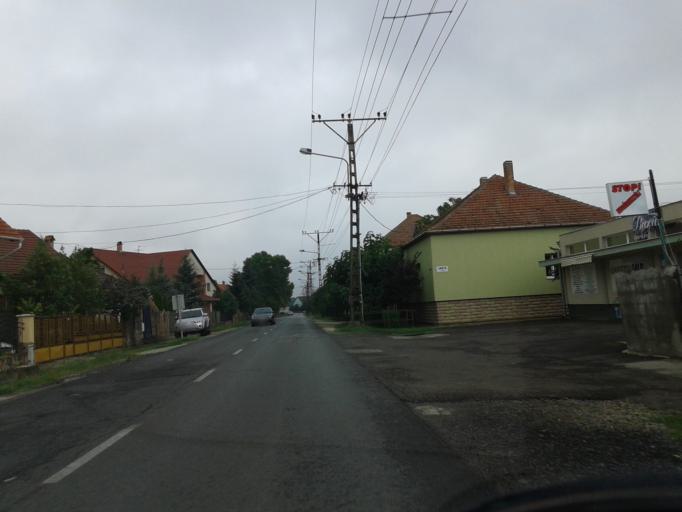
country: HU
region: Csongrad
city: Szeged
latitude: 46.2585
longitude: 20.1867
